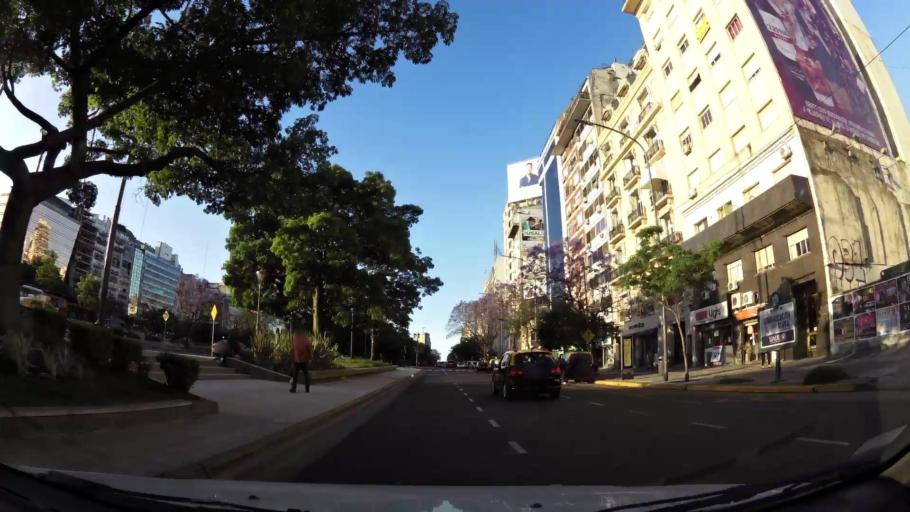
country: AR
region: Buenos Aires F.D.
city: Retiro
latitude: -34.5973
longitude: -58.3815
